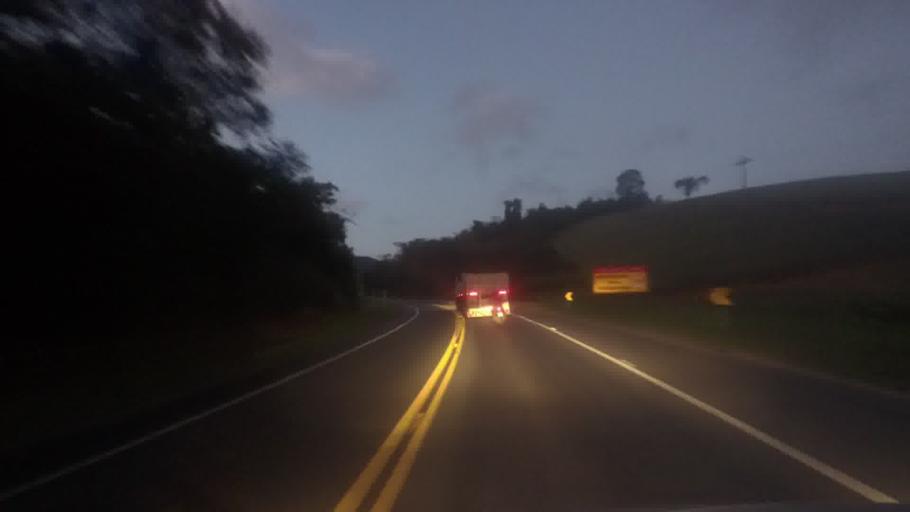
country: BR
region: Espirito Santo
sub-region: Iconha
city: Iconha
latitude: -20.7703
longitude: -40.7607
